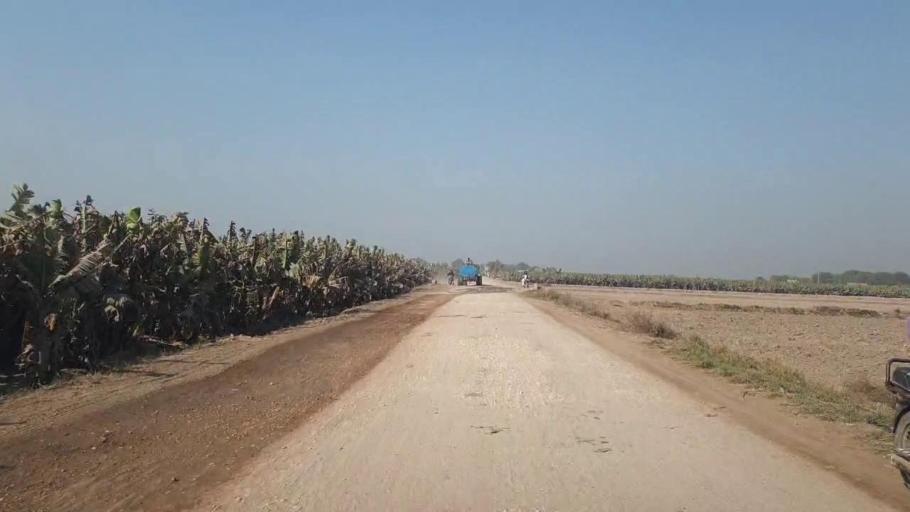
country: PK
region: Sindh
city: Tando Allahyar
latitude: 25.3627
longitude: 68.6565
